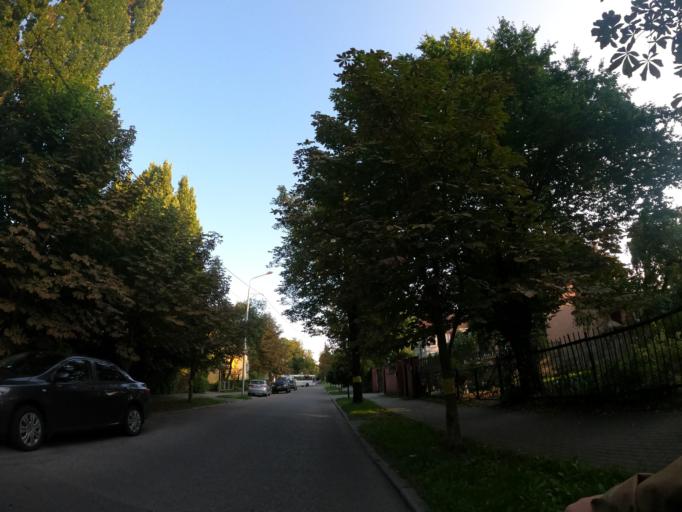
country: RU
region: Kaliningrad
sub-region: Gorod Kaliningrad
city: Kaliningrad
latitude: 54.7187
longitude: 20.4651
